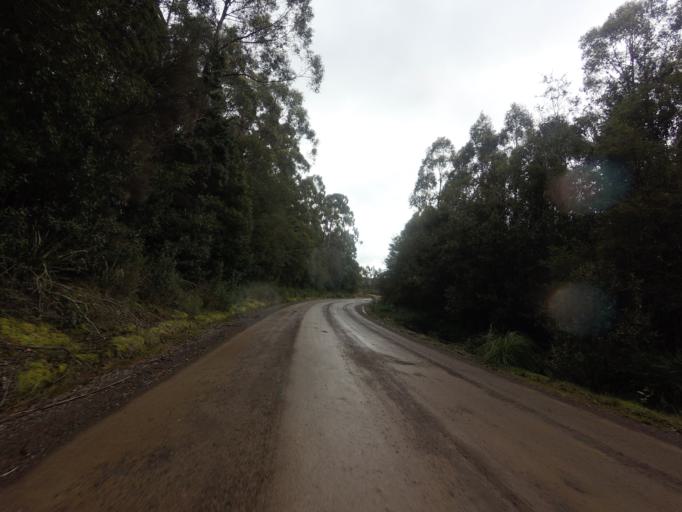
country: AU
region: Tasmania
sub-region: Huon Valley
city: Geeveston
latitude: -43.4775
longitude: 146.8911
